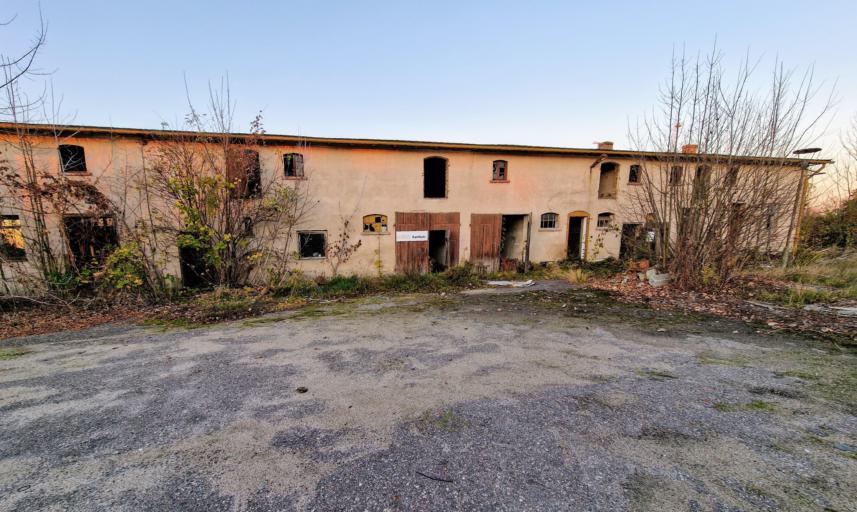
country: PL
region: Lubusz
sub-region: Powiat miedzyrzecki
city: Miedzyrzecz
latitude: 52.4435
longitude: 15.5973
